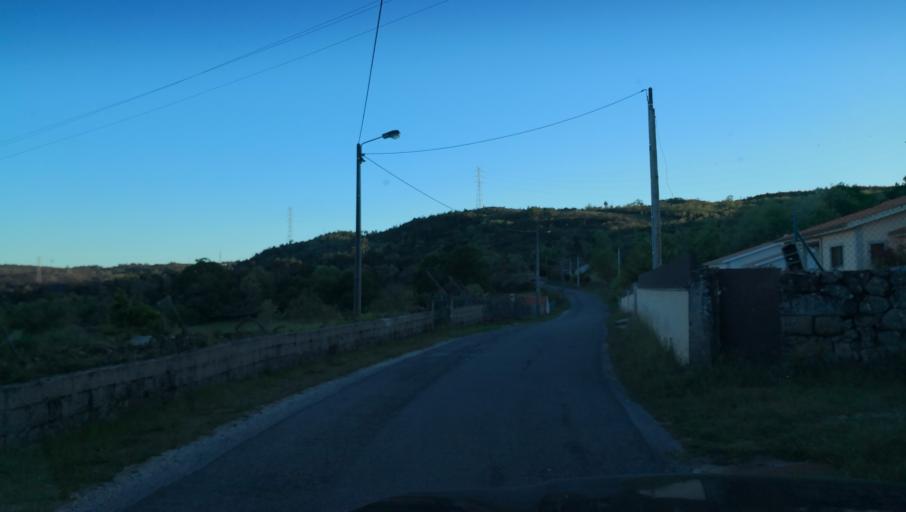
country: PT
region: Vila Real
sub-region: Sabrosa
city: Sabrosa
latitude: 41.3452
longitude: -7.6212
